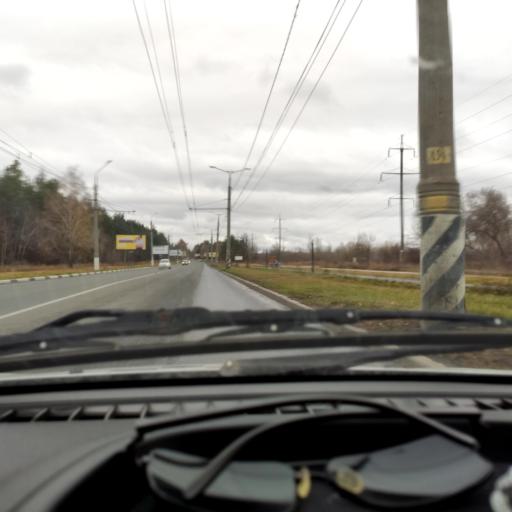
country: RU
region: Samara
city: Tol'yatti
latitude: 53.4980
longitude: 49.3883
